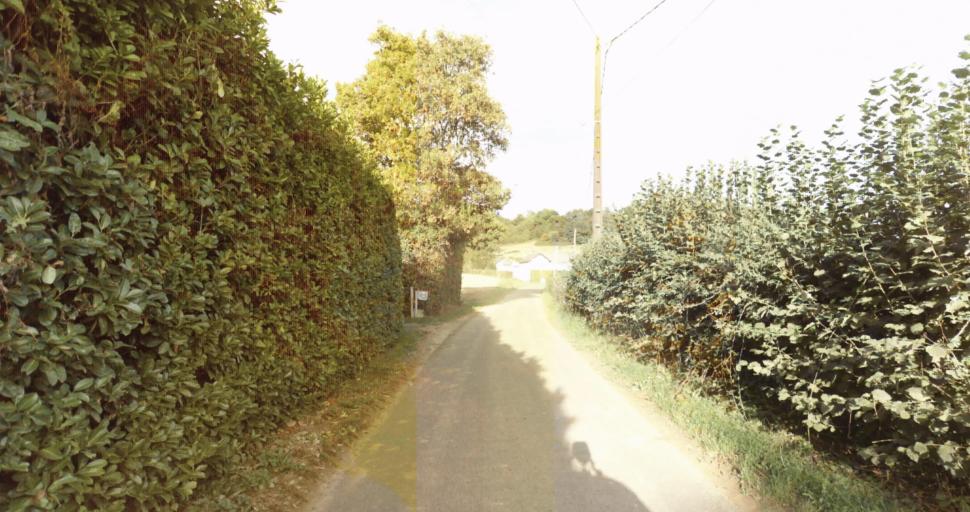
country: FR
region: Lower Normandy
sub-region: Departement de l'Orne
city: Gace
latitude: 48.7140
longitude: 0.3122
